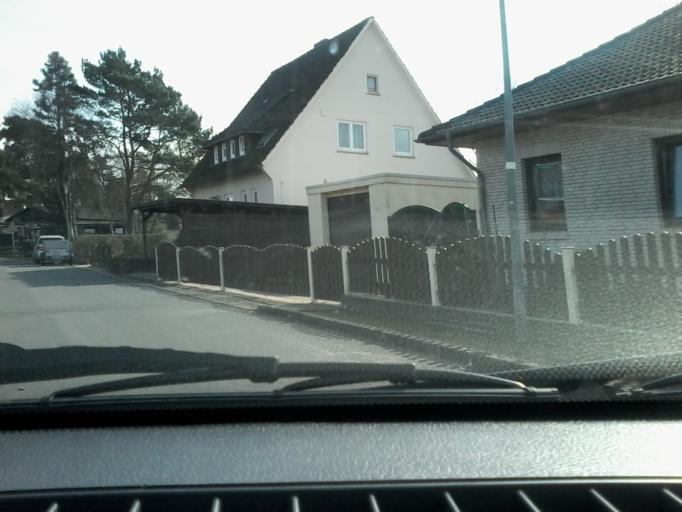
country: DE
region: Lower Saxony
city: Achim
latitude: 53.0035
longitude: 9.0413
